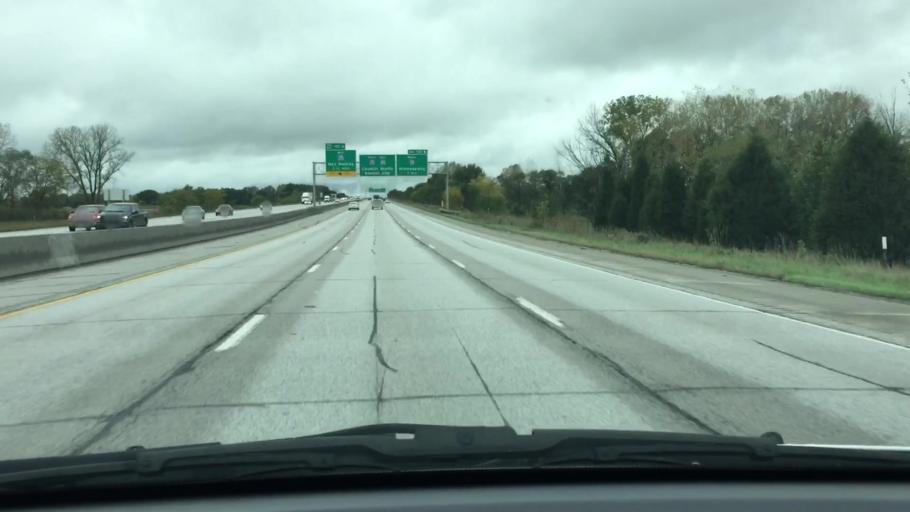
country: US
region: Iowa
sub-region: Polk County
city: Pleasant Hill
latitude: 41.6561
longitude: -93.5490
